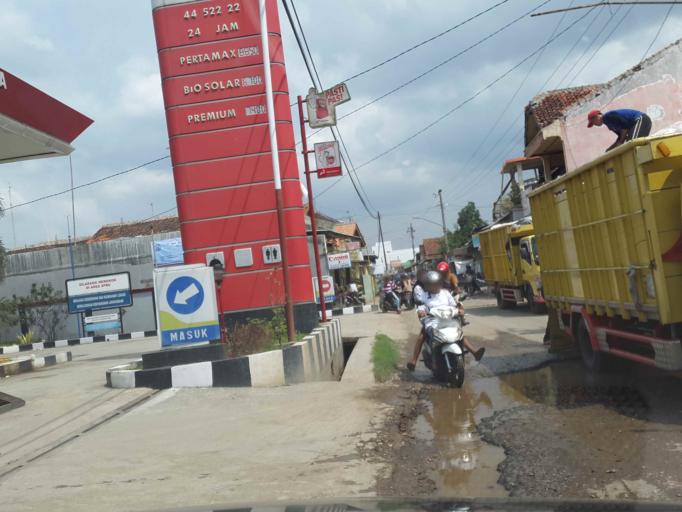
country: ID
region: Central Java
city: Ketanggungan
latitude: -6.9371
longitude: 108.8829
